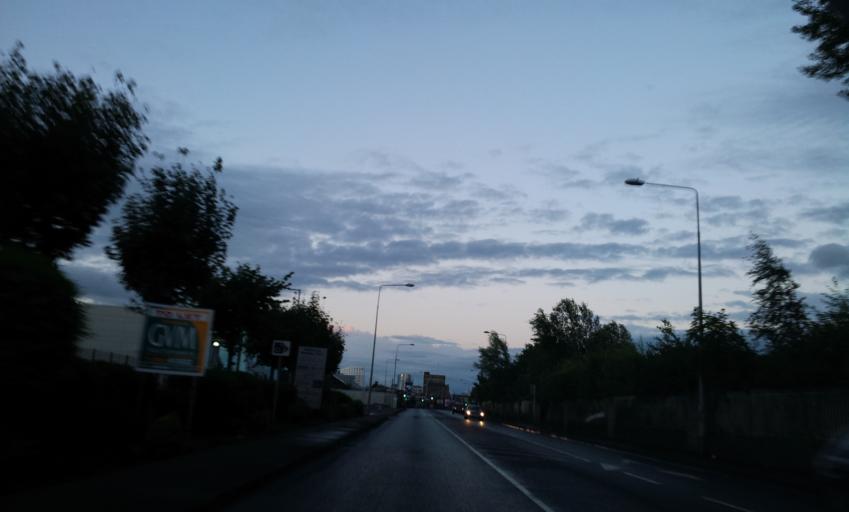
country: IE
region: Munster
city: Moyross
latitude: 52.6548
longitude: -8.6515
